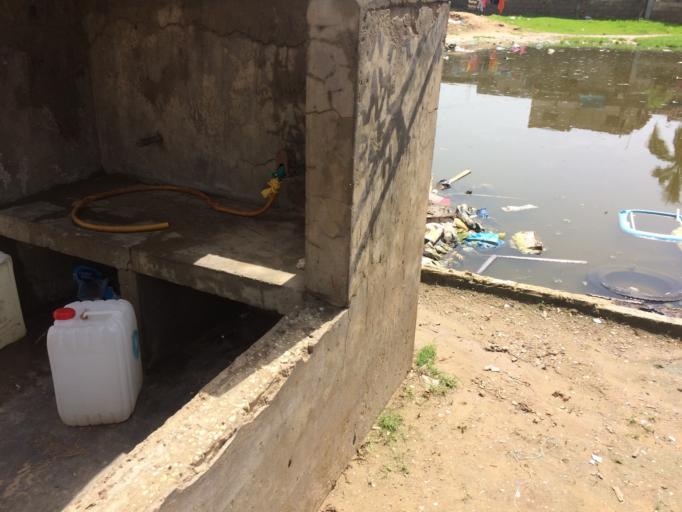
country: SN
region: Dakar
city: Pikine
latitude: 14.7323
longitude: -17.3249
